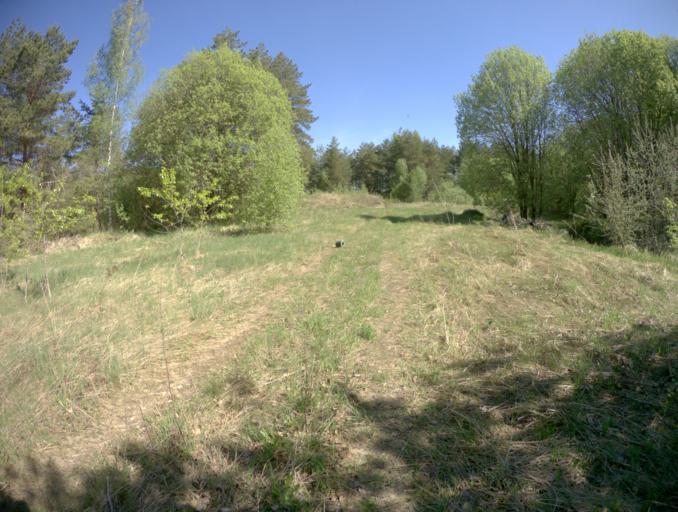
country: RU
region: Ivanovo
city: Gavrilov Posad
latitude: 56.4269
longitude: 40.2004
